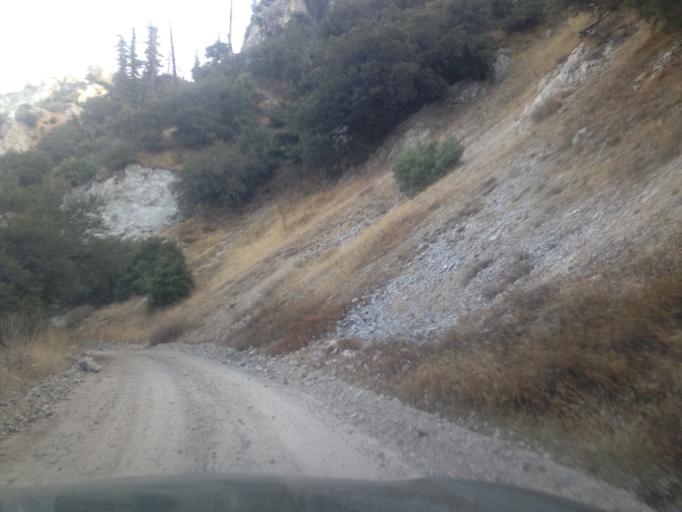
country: US
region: California
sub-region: San Bernardino County
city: Yucaipa
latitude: 34.1198
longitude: -117.0267
